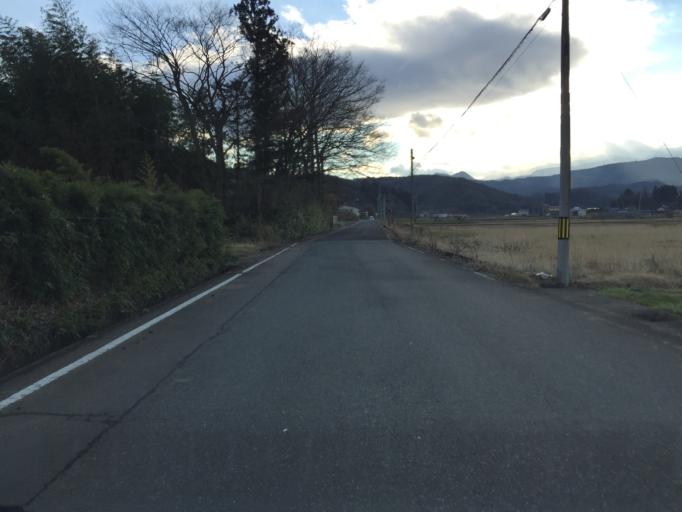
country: JP
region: Fukushima
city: Fukushima-shi
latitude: 37.7109
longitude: 140.4421
